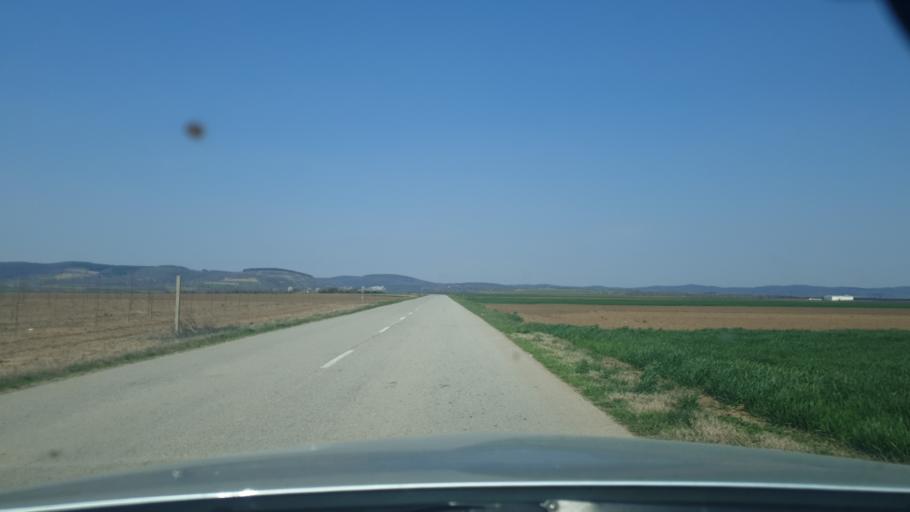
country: RS
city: Vrdnik
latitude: 45.0794
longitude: 19.7697
